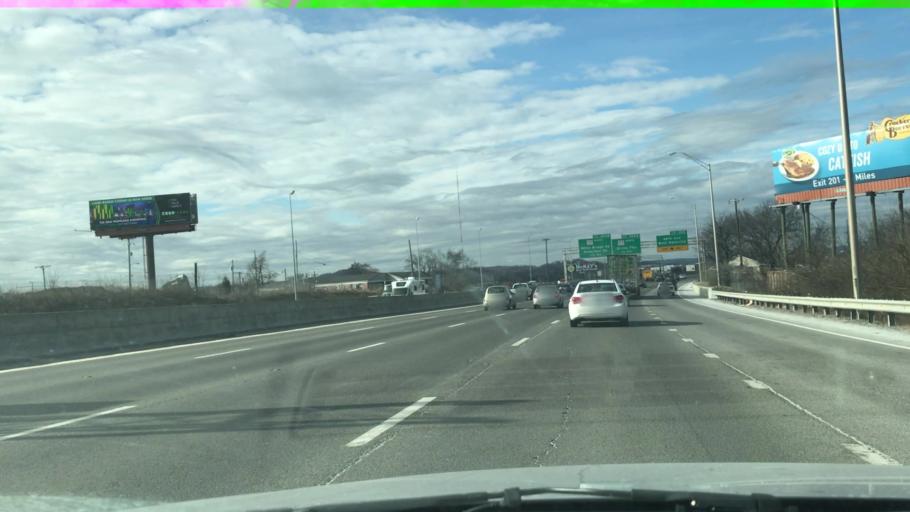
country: US
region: Tennessee
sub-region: Davidson County
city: Nashville
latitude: 36.1548
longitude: -86.8318
